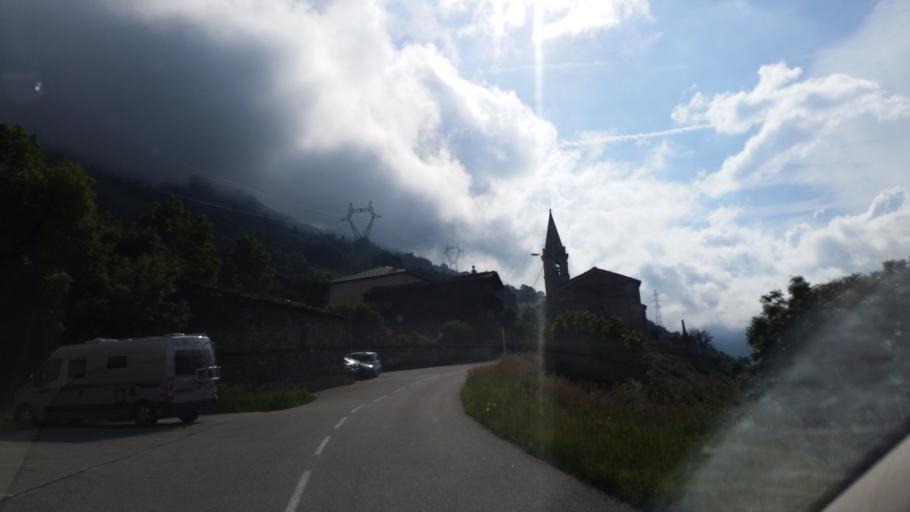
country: FR
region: Rhone-Alpes
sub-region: Departement de la Savoie
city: Modane
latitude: 45.2090
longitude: 6.6002
